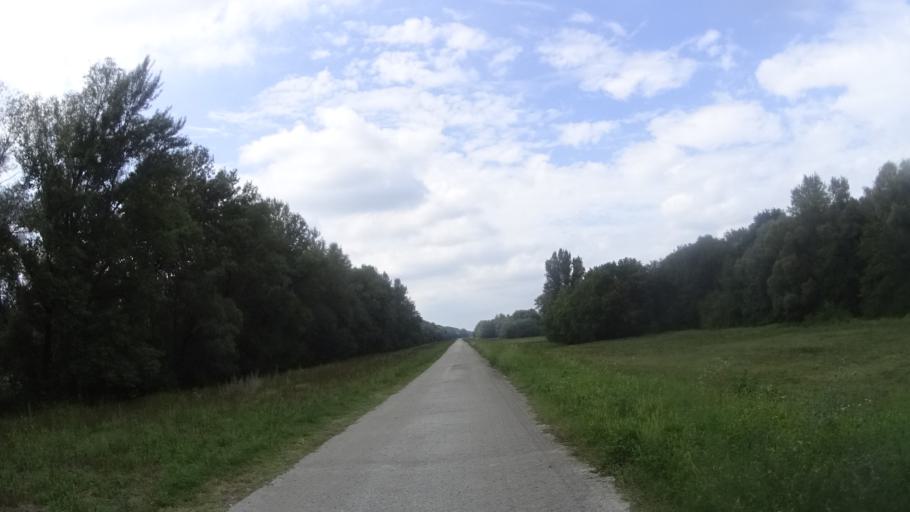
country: SK
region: Trnavsky
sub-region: Okres Dunajska Streda
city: Velky Meder
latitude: 47.7692
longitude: 17.7185
